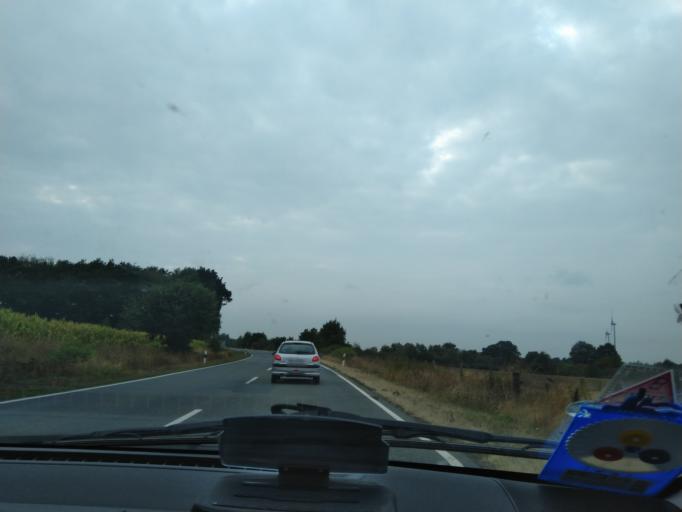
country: DE
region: Lower Saxony
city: Rhede
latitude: 53.0668
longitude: 7.2312
